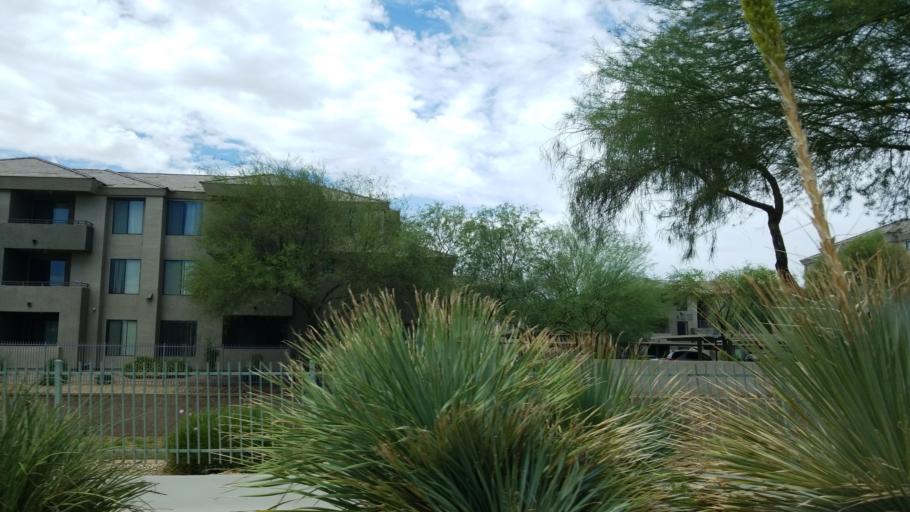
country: US
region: Arizona
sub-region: Maricopa County
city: Anthem
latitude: 33.7071
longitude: -112.1089
